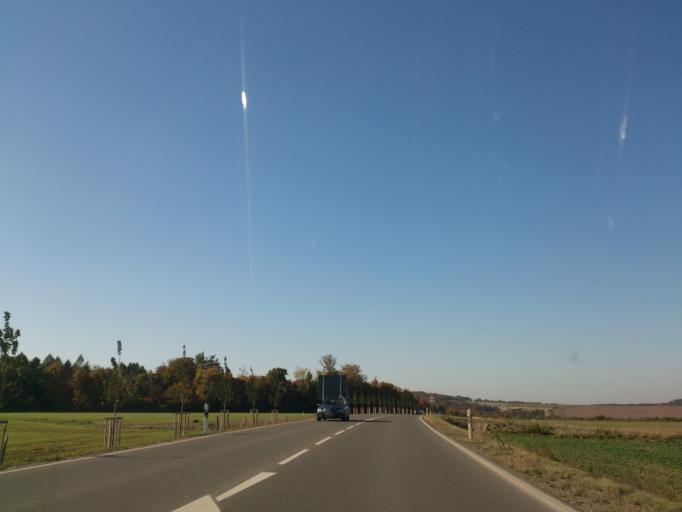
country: DE
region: Hesse
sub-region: Regierungsbezirk Kassel
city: Calden
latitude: 51.4161
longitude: 9.3760
